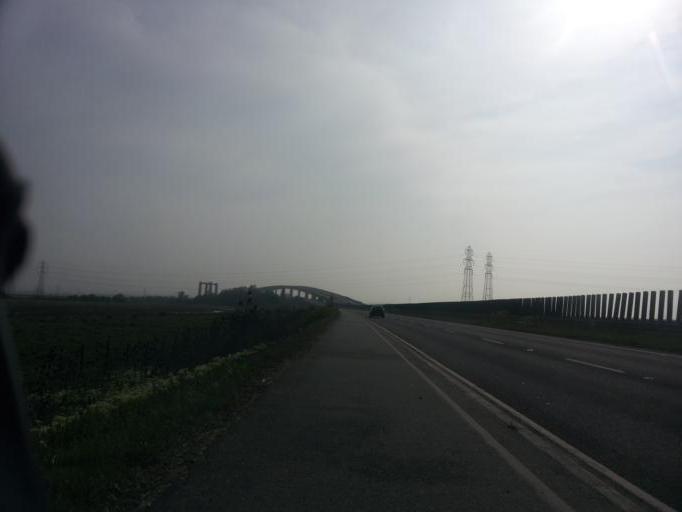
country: GB
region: England
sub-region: Kent
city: Queenborough
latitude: 51.3981
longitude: 0.7607
